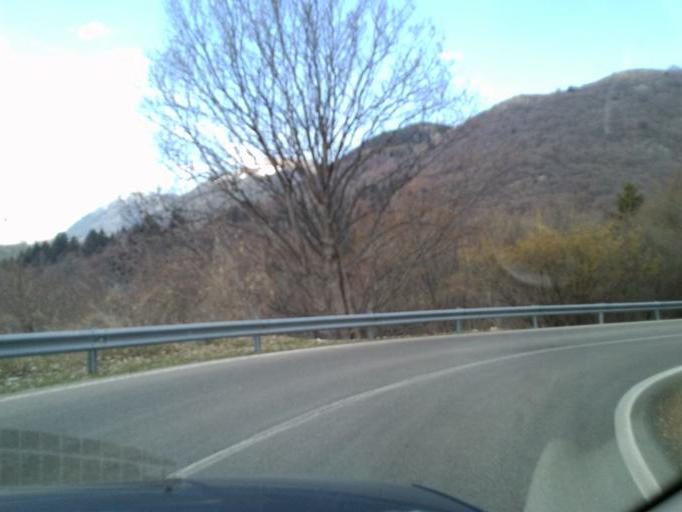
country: IT
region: Veneto
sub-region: Provincia di Verona
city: Erbezzo
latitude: 45.6532
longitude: 10.9805
